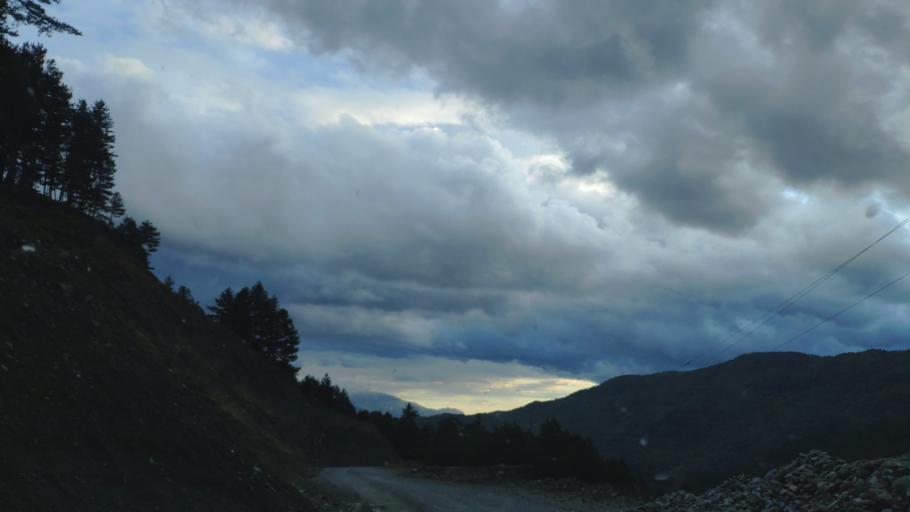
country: AL
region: Korce
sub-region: Rrethi i Kolonjes
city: Erseke
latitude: 40.2847
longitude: 20.8610
